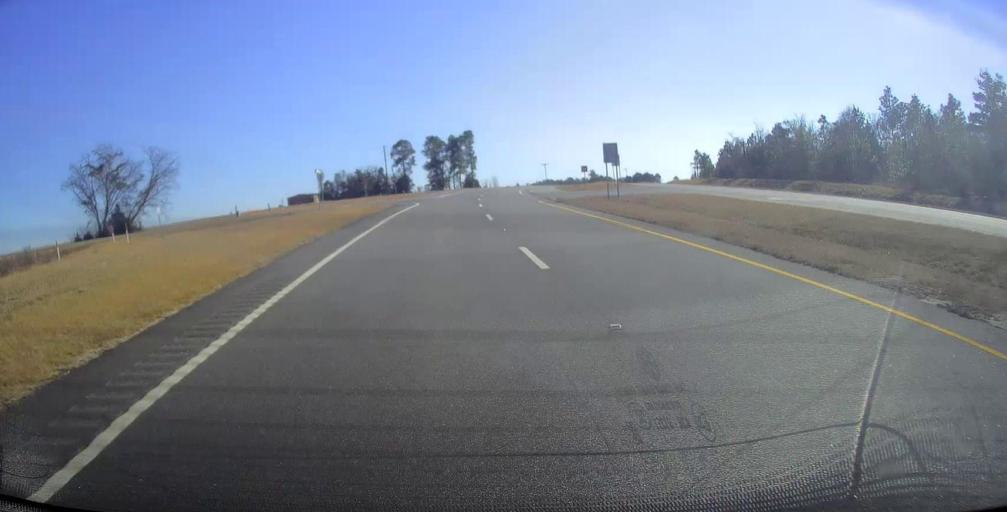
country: US
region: Georgia
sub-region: Taylor County
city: Butler
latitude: 32.6092
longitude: -84.2372
